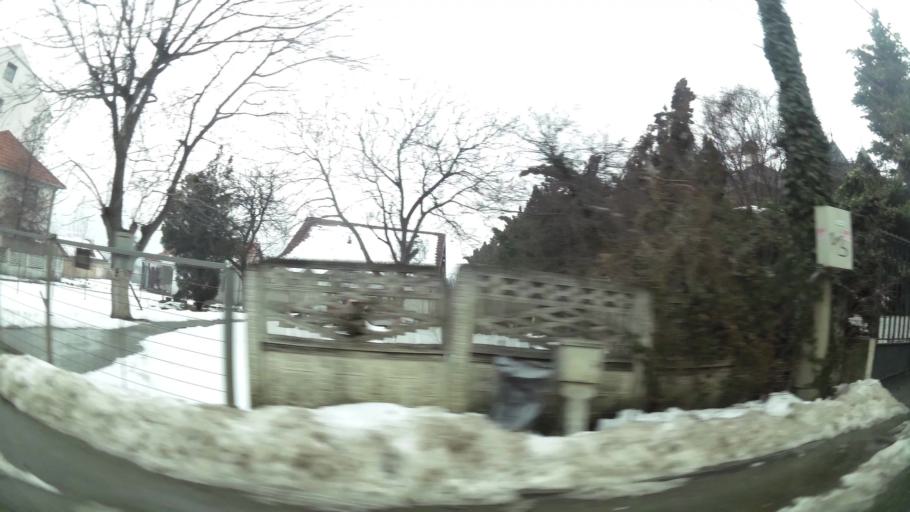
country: RS
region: Central Serbia
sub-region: Belgrade
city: Zvezdara
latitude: 44.7697
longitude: 20.5131
